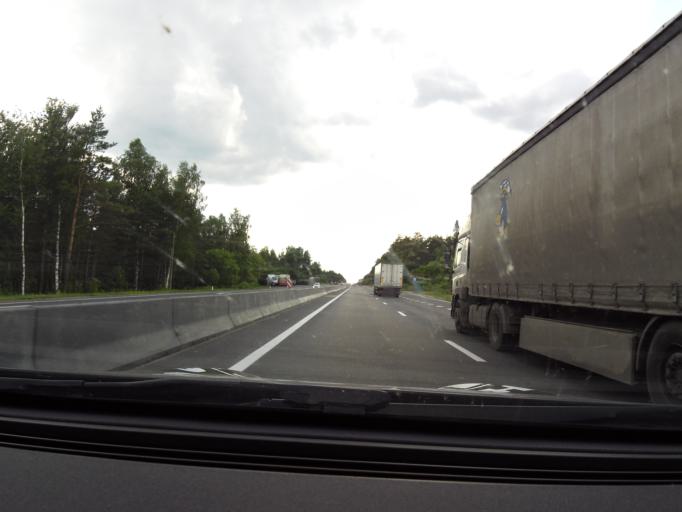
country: RU
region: Nizjnij Novgorod
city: Yuganets
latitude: 56.2875
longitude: 43.2197
